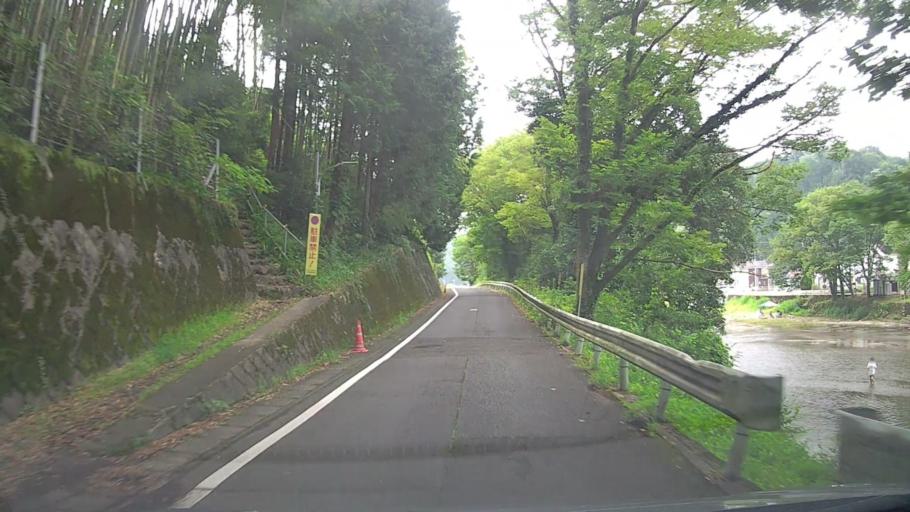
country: JP
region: Tokyo
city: Itsukaichi
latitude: 35.7249
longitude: 139.2217
